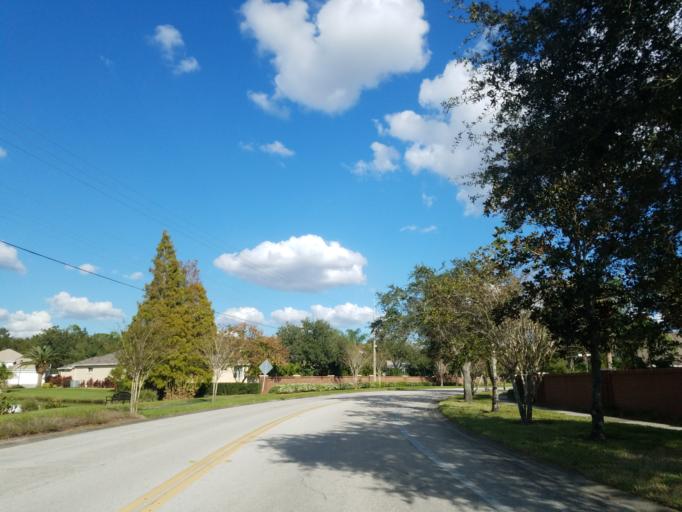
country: US
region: Florida
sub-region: Hillsborough County
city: Riverview
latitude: 27.8804
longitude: -82.3369
